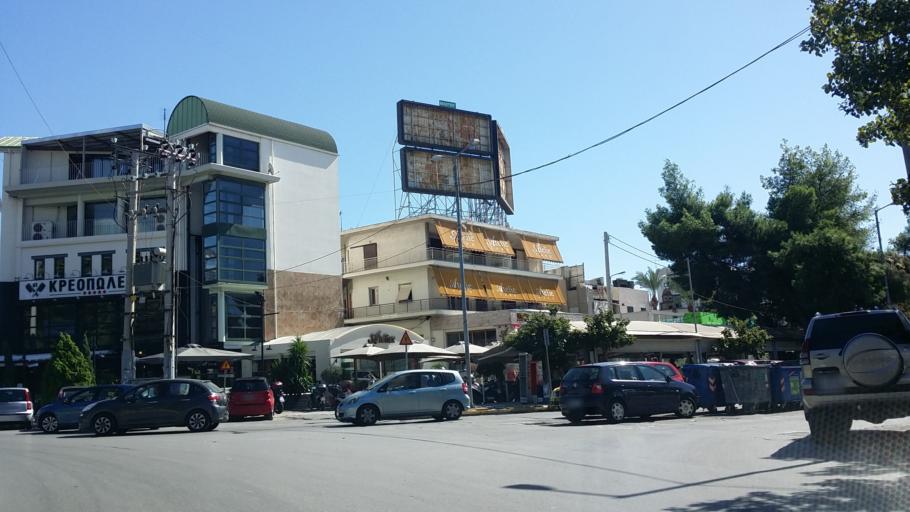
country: GR
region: Attica
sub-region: Nomarchia Athinas
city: Peristeri
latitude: 38.0124
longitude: 23.7064
